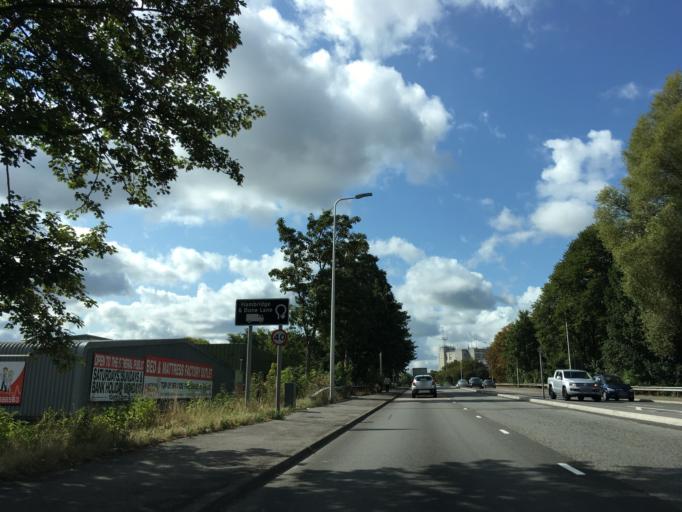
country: GB
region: England
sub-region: West Berkshire
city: Newbury
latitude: 51.4034
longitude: -1.3188
